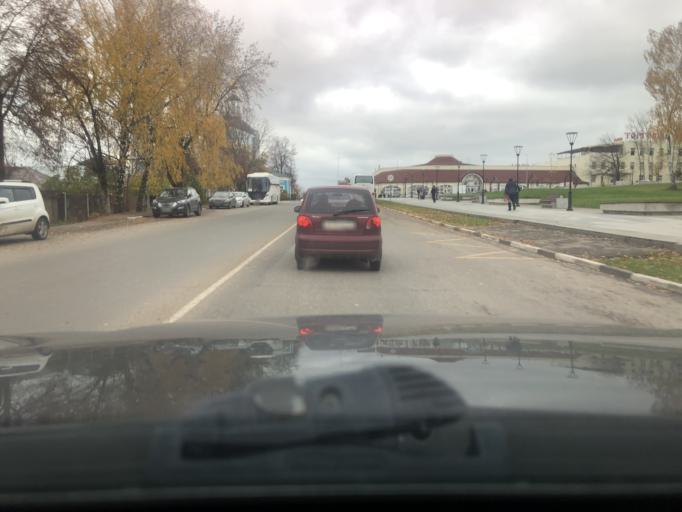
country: RU
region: Moskovskaya
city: Sergiyev Posad
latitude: 56.3142
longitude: 38.1316
